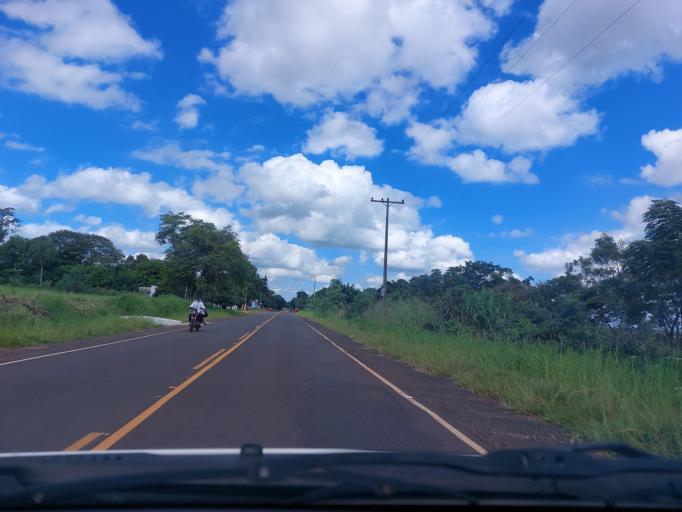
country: PY
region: San Pedro
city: Guayaybi
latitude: -24.5909
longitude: -56.5196
